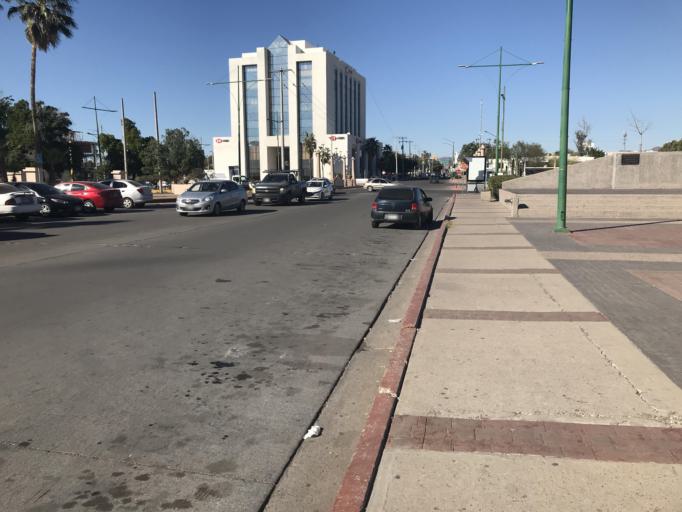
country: MX
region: Sonora
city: Hermosillo
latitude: 29.0683
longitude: -110.9578
